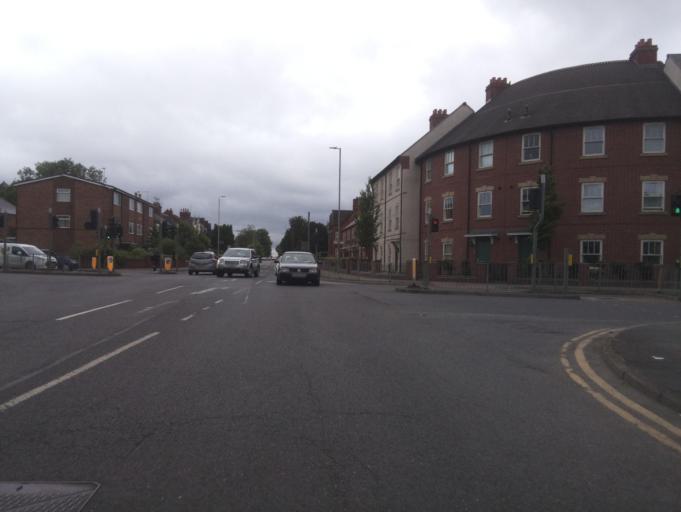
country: GB
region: England
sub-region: Leicestershire
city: Coalville
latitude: 52.7207
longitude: -1.3599
